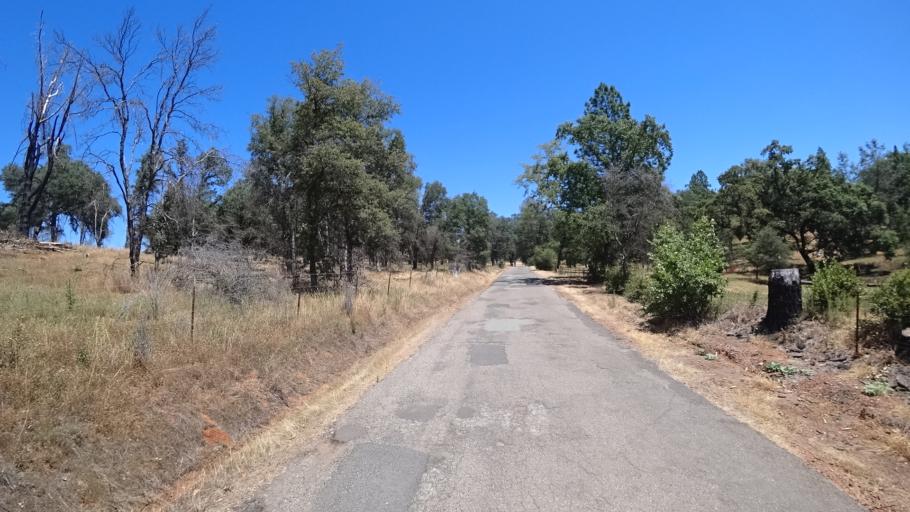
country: US
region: California
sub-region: Calaveras County
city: Mountain Ranch
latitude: 38.2902
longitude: -120.6034
